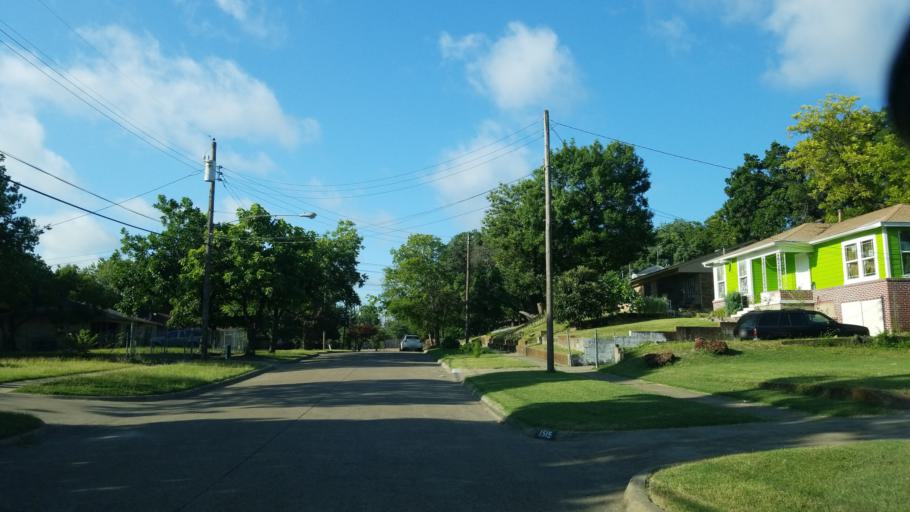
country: US
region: Texas
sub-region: Dallas County
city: Dallas
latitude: 32.7291
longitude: -96.8103
